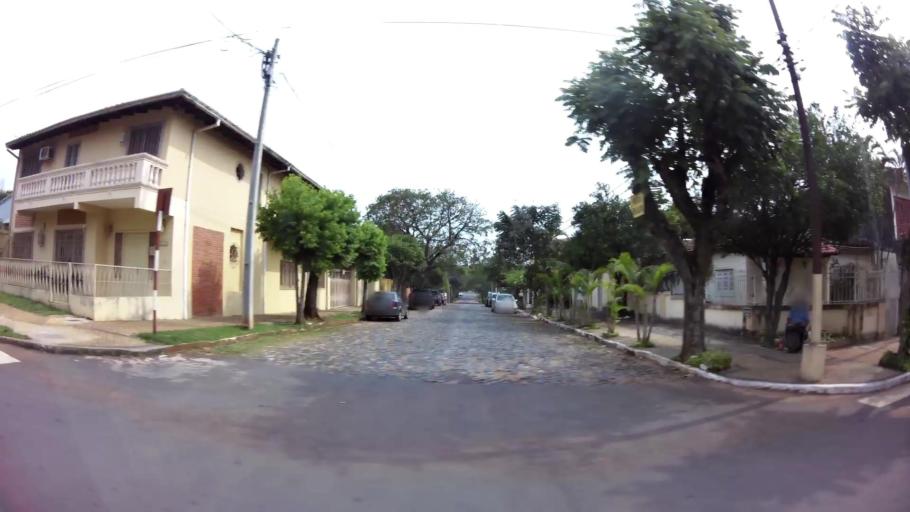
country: PY
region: Central
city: Lambare
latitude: -25.2944
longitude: -57.5699
